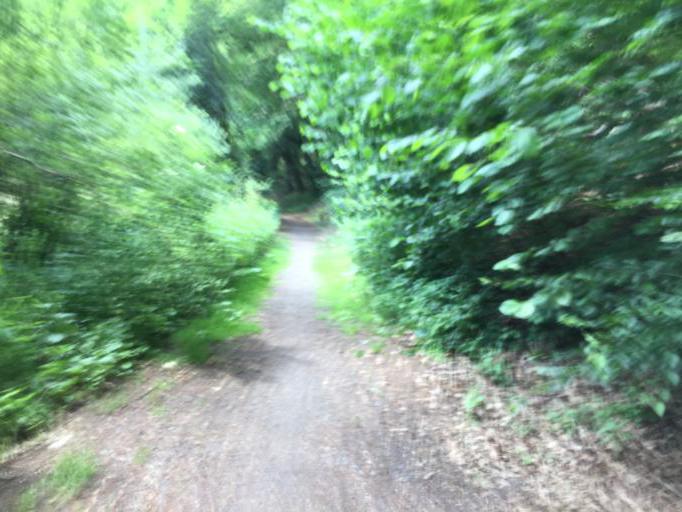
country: DE
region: Rheinland-Pfalz
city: Heiligenroth
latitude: 50.4315
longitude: 7.8702
